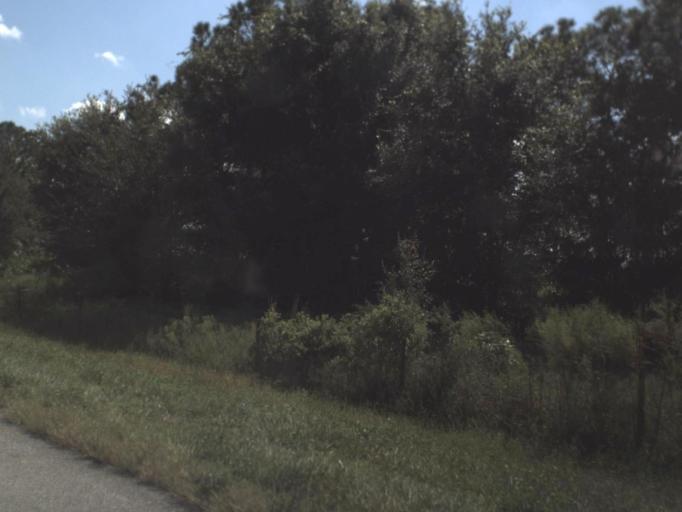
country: US
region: Florida
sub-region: Highlands County
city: Sebring
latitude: 27.4132
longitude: -81.5610
